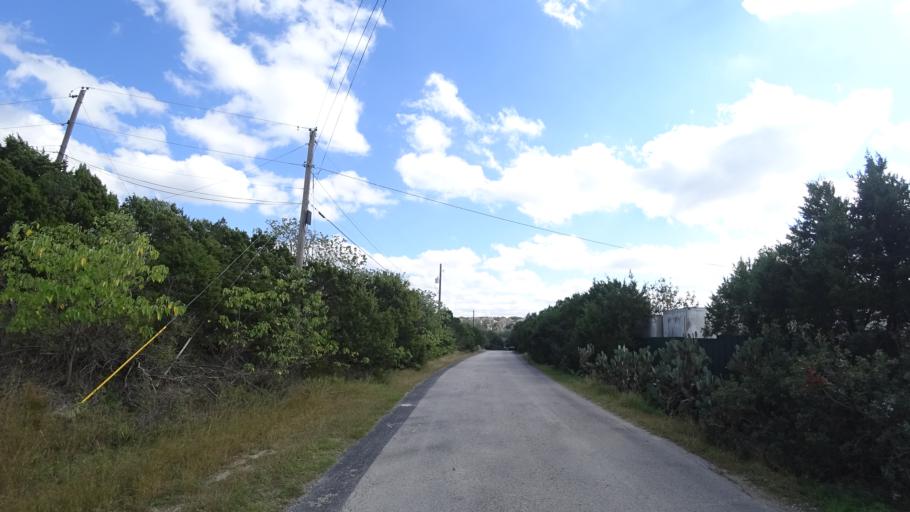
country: US
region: Texas
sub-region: Travis County
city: Barton Creek
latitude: 30.2582
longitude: -97.8901
